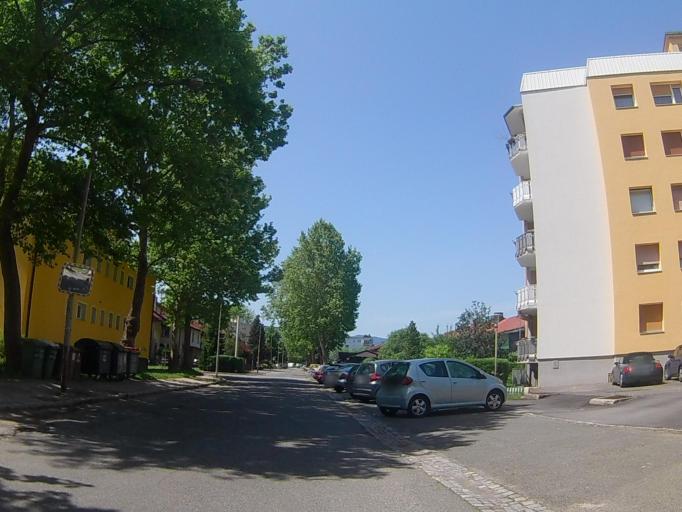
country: SI
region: Maribor
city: Maribor
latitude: 46.5660
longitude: 15.6367
